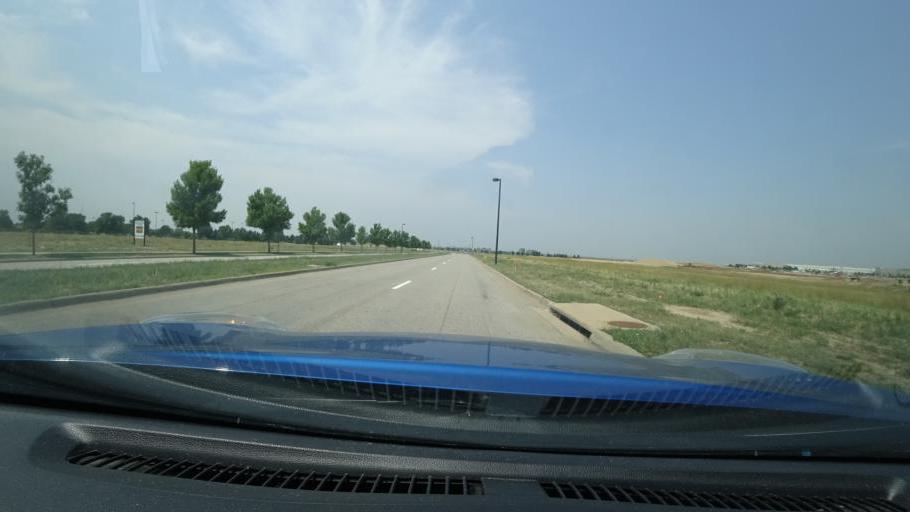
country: US
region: Colorado
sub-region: Adams County
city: Aurora
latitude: 39.7652
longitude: -104.7779
